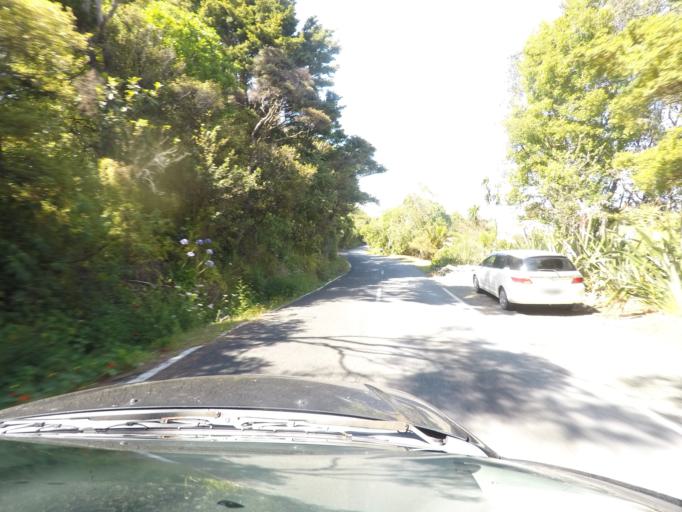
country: NZ
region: Auckland
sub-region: Auckland
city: Warkworth
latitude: -36.3139
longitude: 174.7912
